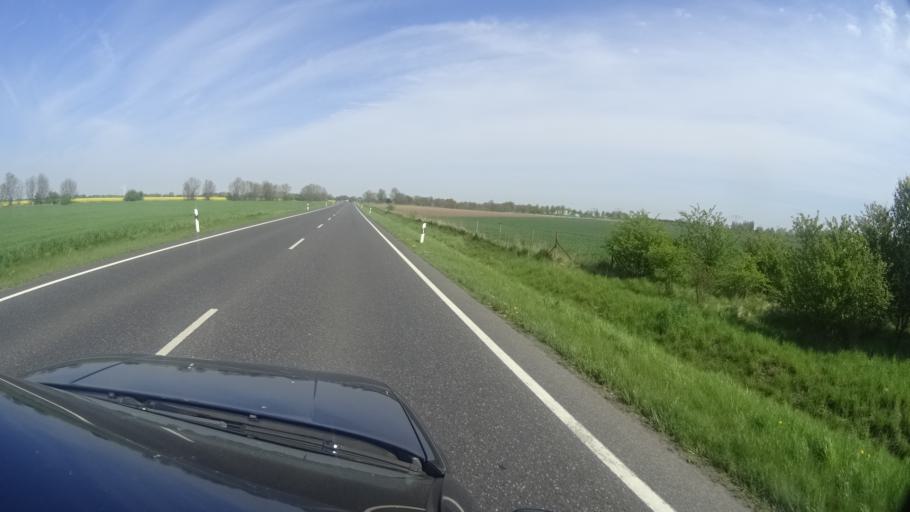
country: DE
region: Brandenburg
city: Nauen
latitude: 52.6045
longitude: 12.8478
